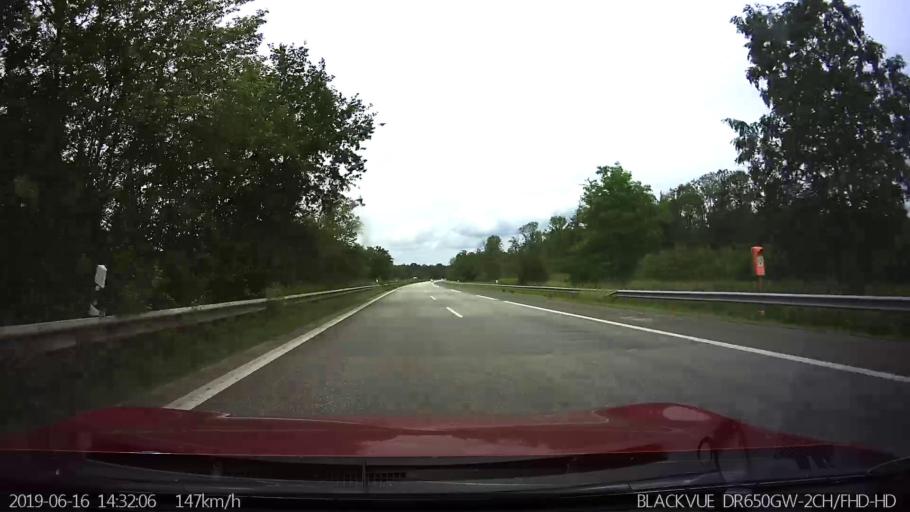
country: DE
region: Schleswig-Holstein
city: Schonbek
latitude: 54.1818
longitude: 9.9583
